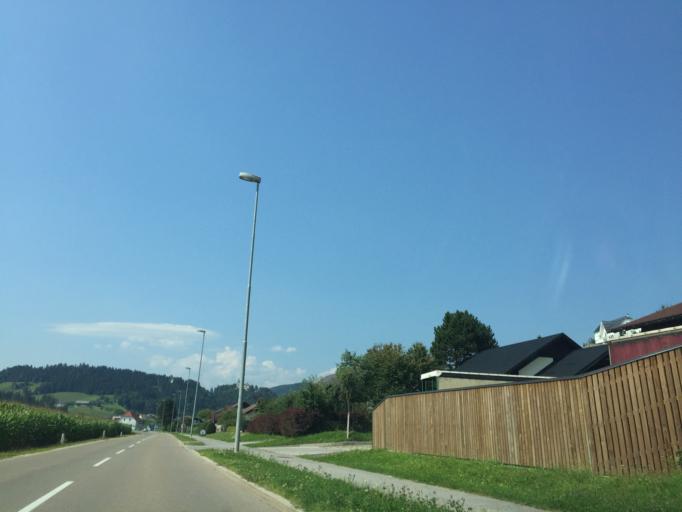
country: SI
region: Slovenj Gradec
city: Slovenj Gradec
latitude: 46.4919
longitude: 15.0735
